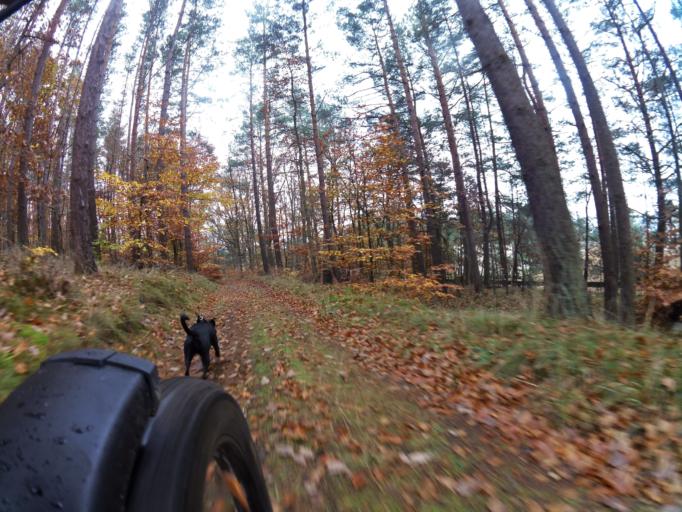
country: PL
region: Pomeranian Voivodeship
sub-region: Powiat pucki
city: Krokowa
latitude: 54.7454
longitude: 18.0948
